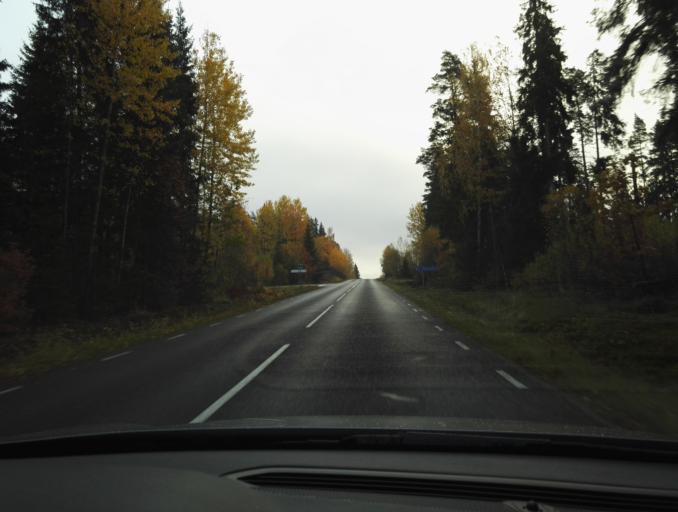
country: SE
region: Kronoberg
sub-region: Alvesta Kommun
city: Moheda
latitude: 57.0090
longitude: 14.7206
